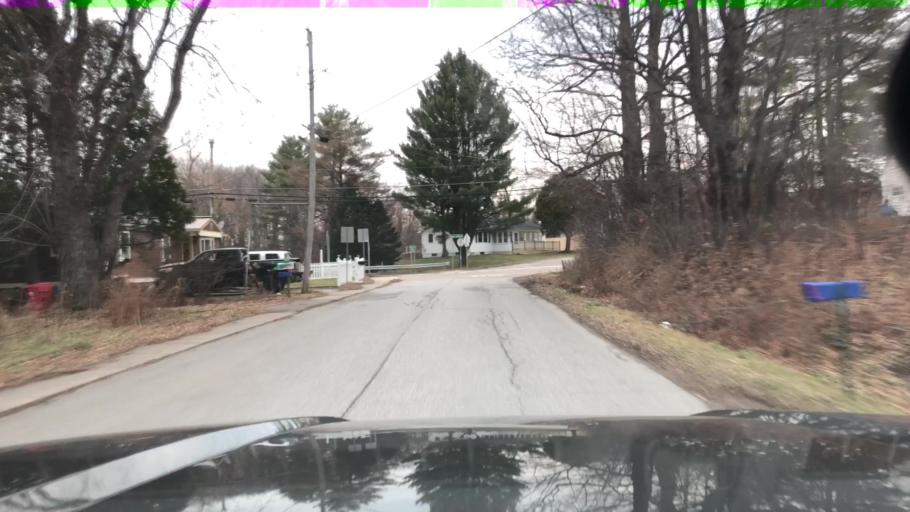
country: US
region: Vermont
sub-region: Chittenden County
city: Essex Junction
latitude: 44.5118
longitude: -73.0572
